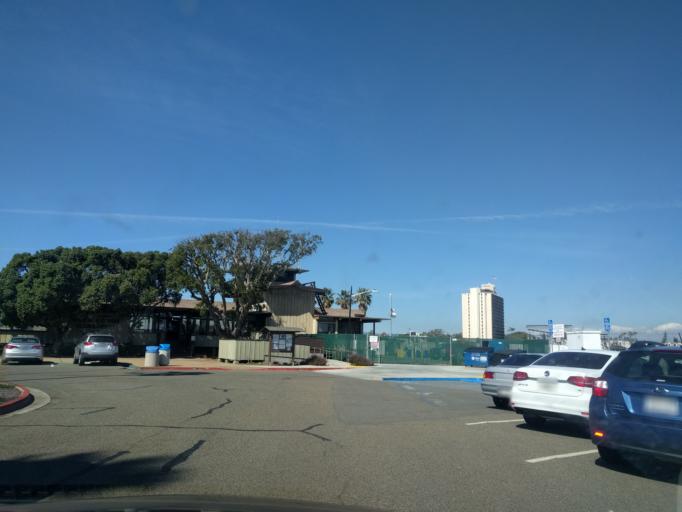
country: US
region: California
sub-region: San Diego County
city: La Jolla
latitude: 32.7610
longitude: -117.2410
